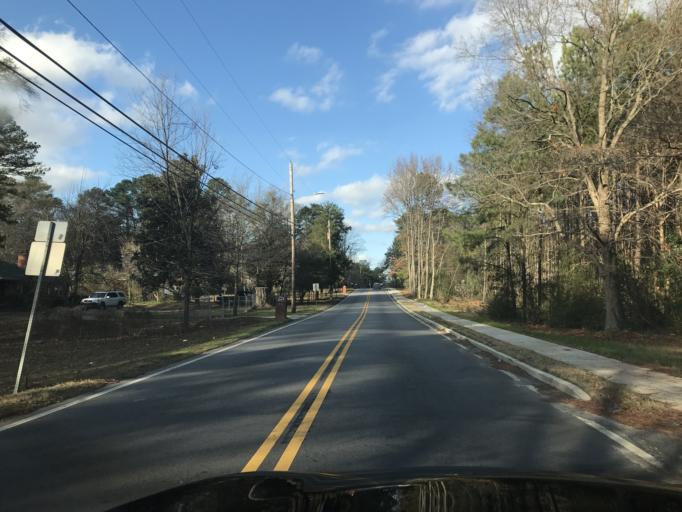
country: US
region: Georgia
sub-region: Fulton County
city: College Park
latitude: 33.6312
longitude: -84.4727
